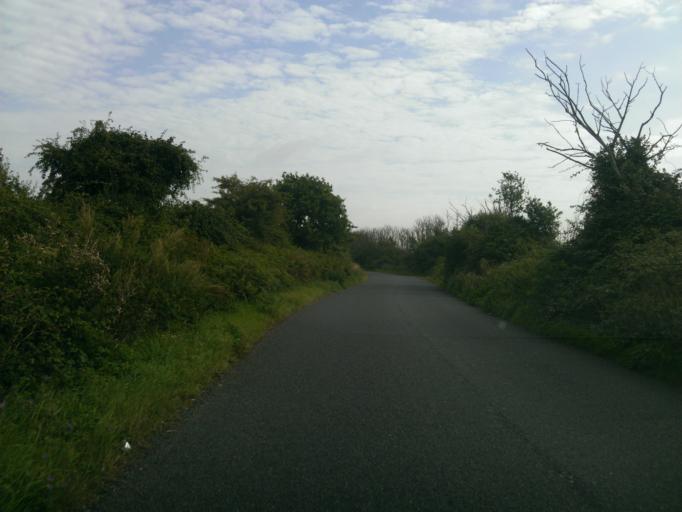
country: GB
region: England
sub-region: Essex
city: Saint Osyth
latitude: 51.8068
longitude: 1.0870
